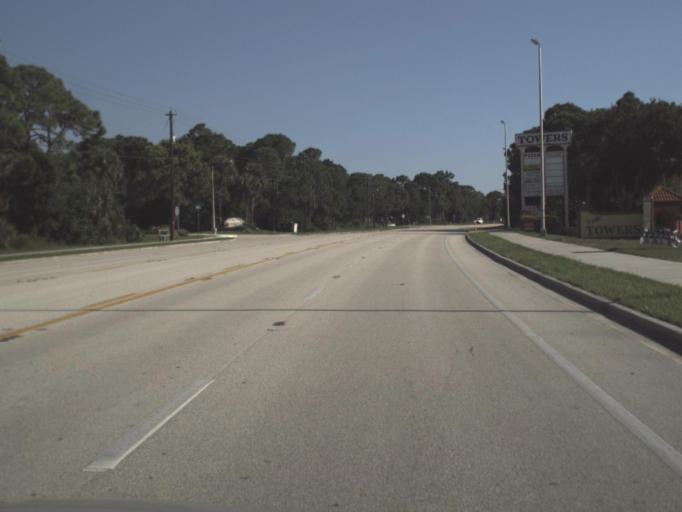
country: US
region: Florida
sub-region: Sarasota County
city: Englewood
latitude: 26.9740
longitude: -82.3542
